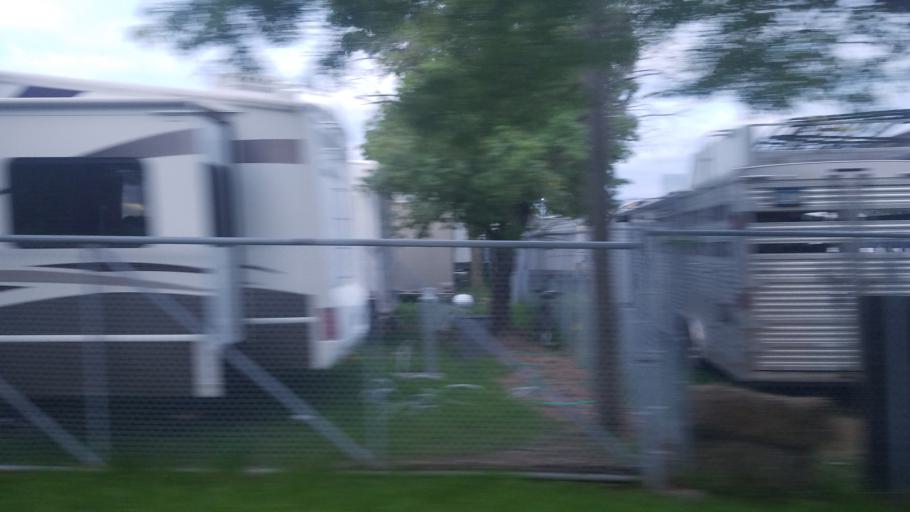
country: US
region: Minnesota
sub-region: Ramsey County
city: Falcon Heights
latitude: 44.9791
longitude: -93.1809
